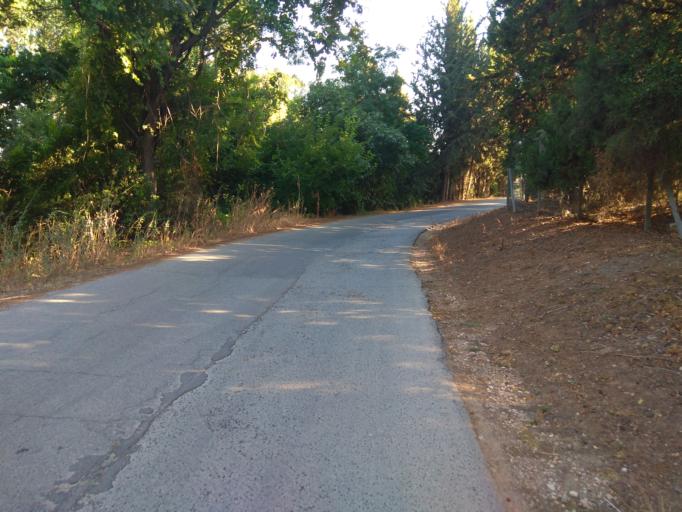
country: IL
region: Northern District
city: Qiryat Shemona
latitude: 33.2219
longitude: 35.6191
